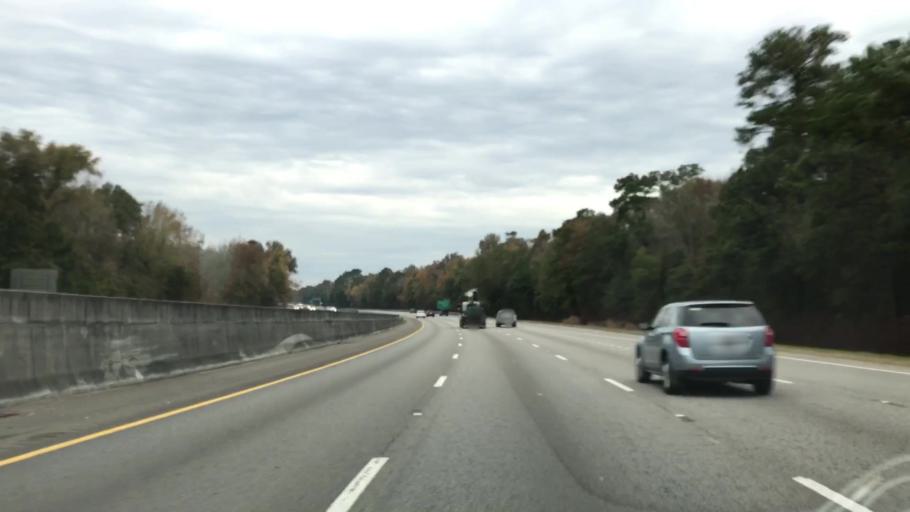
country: US
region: South Carolina
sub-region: Berkeley County
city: Ladson
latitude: 32.9834
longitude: -80.0785
